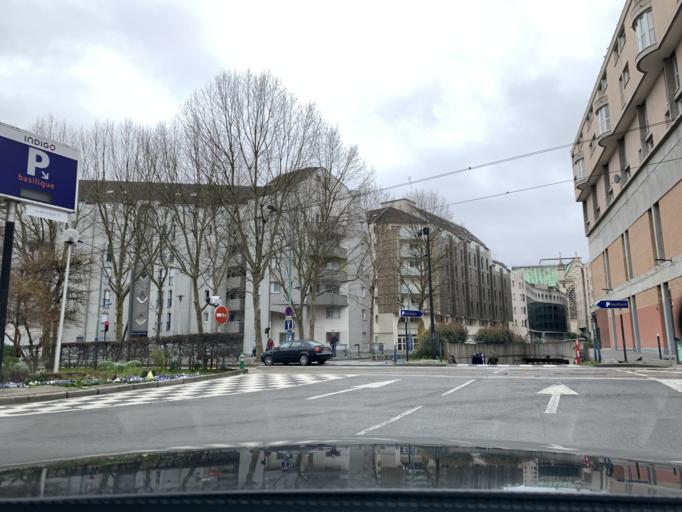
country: FR
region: Ile-de-France
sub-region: Departement de Seine-Saint-Denis
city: Saint-Denis
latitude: 48.9376
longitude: 2.3618
